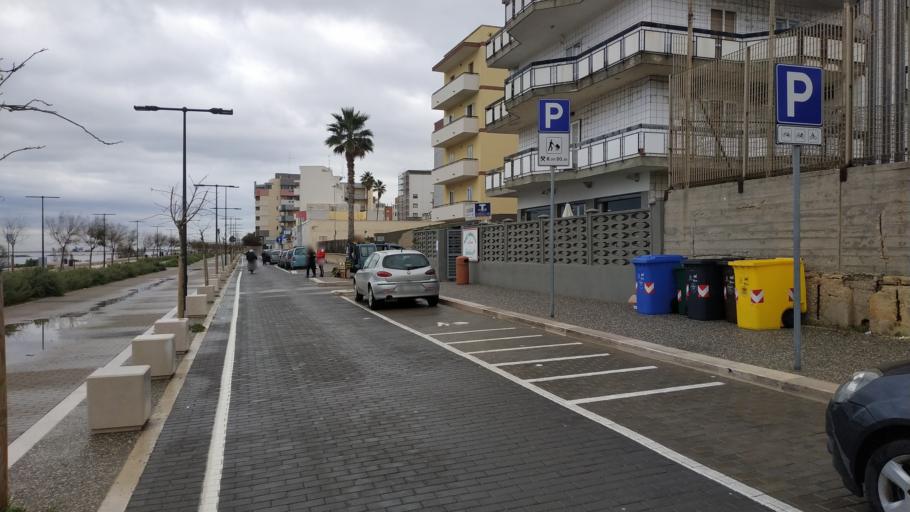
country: IT
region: Apulia
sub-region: Provincia di Bari
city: San Paolo
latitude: 41.1397
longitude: 16.8120
